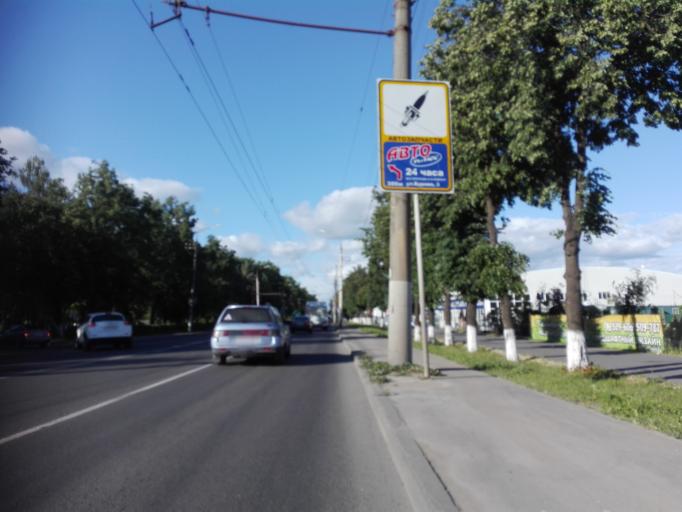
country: RU
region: Orjol
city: Orel
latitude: 53.0031
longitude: 36.1424
